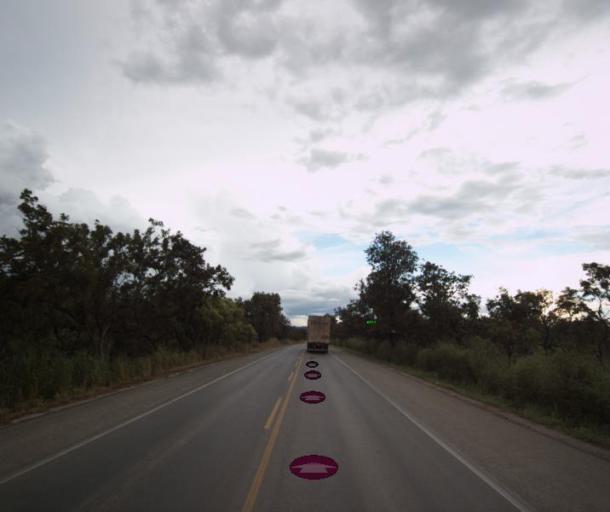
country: BR
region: Goias
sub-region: Itapaci
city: Itapaci
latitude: -14.9497
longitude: -49.3767
